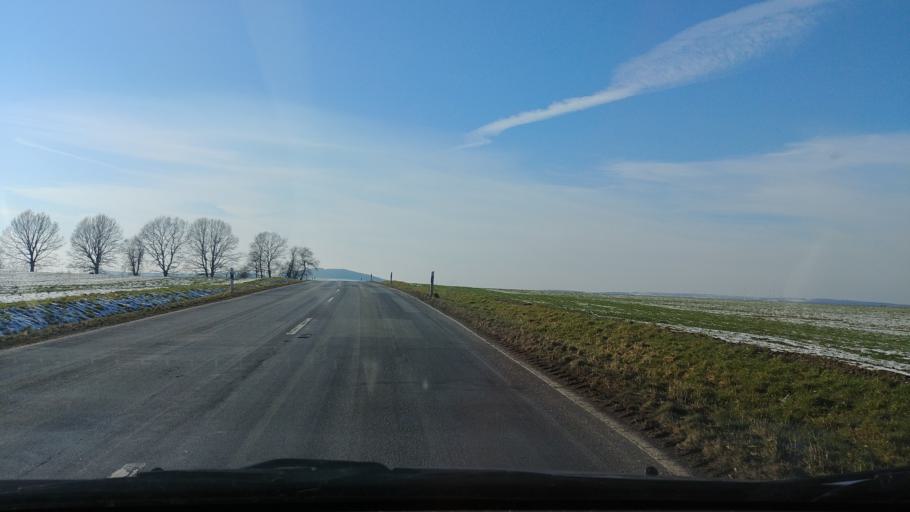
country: DE
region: Hesse
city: Trendelburg
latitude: 51.5737
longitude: 9.4746
